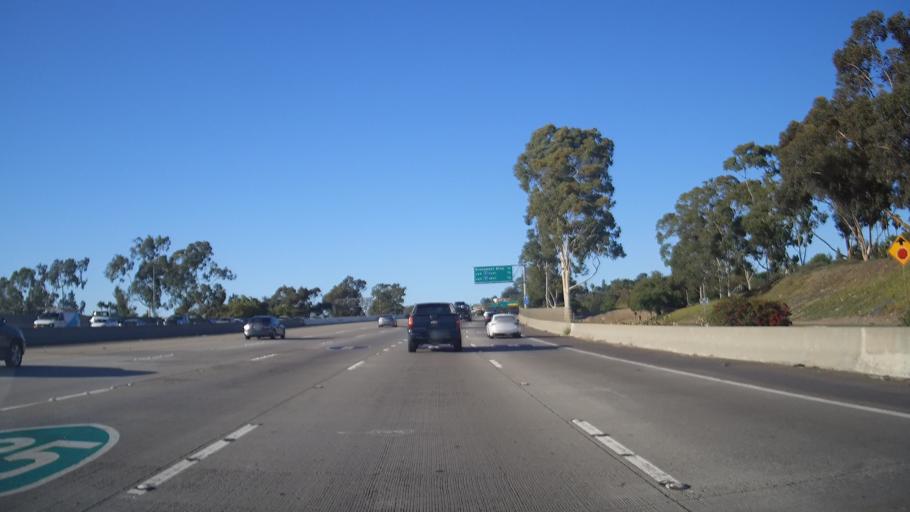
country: US
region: California
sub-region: San Diego County
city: La Mesa
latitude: 32.7663
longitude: -117.0020
